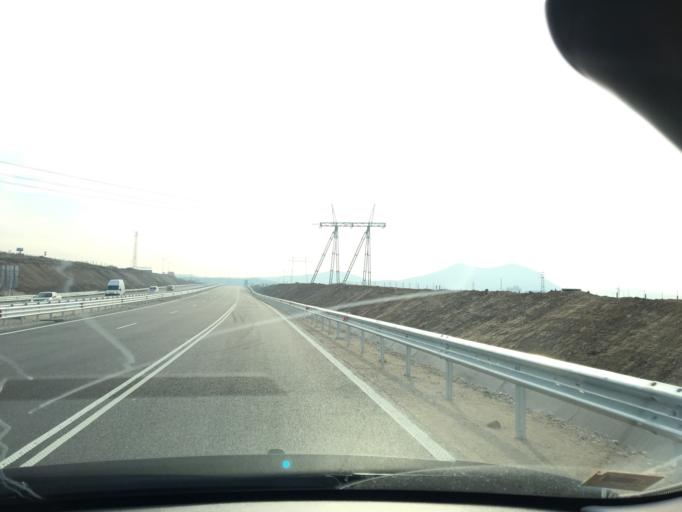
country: BG
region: Blagoevgrad
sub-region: Obshtina Sandanski
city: Sandanski
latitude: 41.5115
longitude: 23.2721
